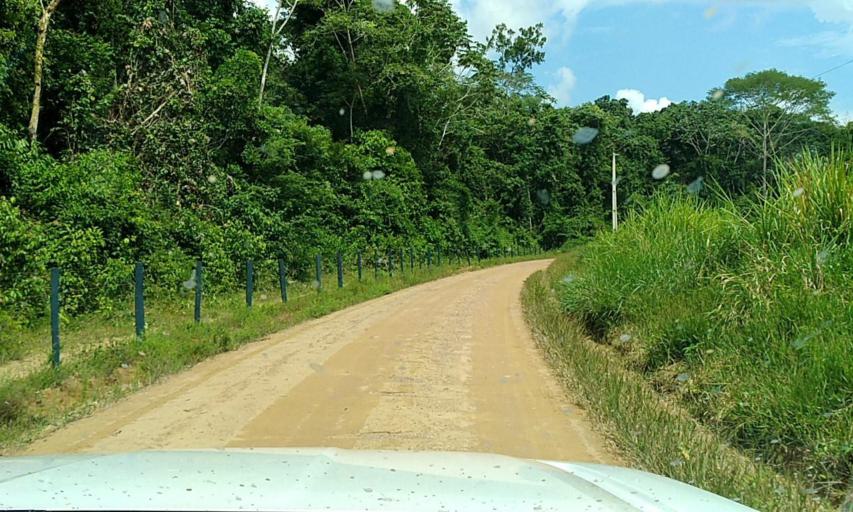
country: BR
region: Para
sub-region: Senador Jose Porfirio
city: Senador Jose Porfirio
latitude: -2.5207
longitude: -51.8353
